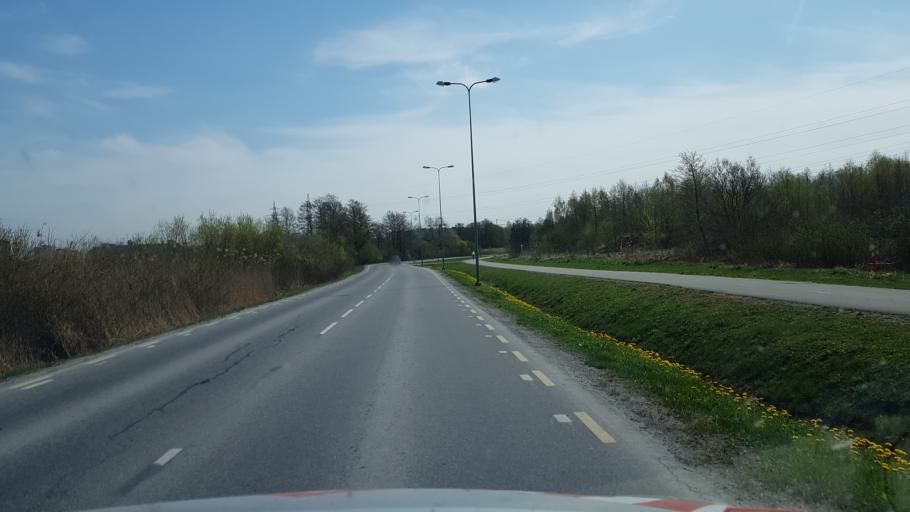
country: EE
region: Harju
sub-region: Saue vald
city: Laagri
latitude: 59.4092
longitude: 24.6143
